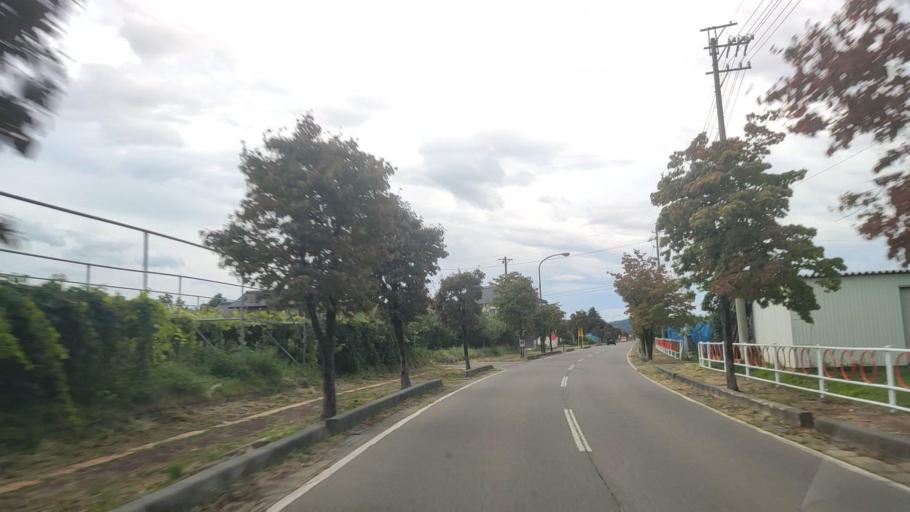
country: JP
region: Nagano
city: Nakano
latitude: 36.7827
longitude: 138.3561
